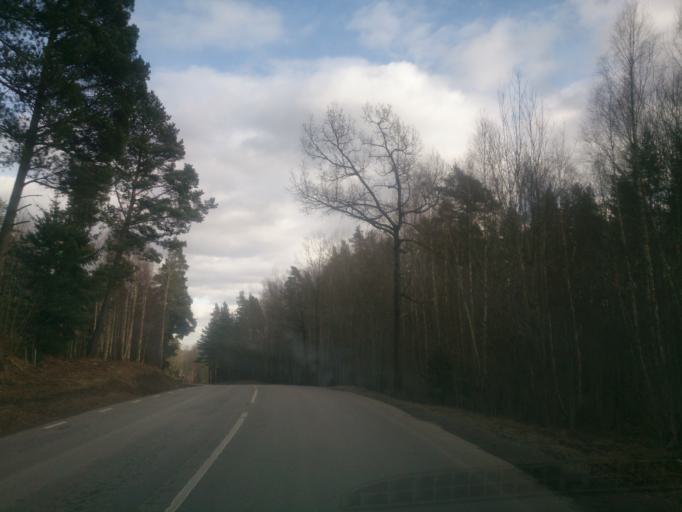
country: SE
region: OEstergoetland
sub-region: Motala Kommun
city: Motala
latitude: 58.5226
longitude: 15.0620
